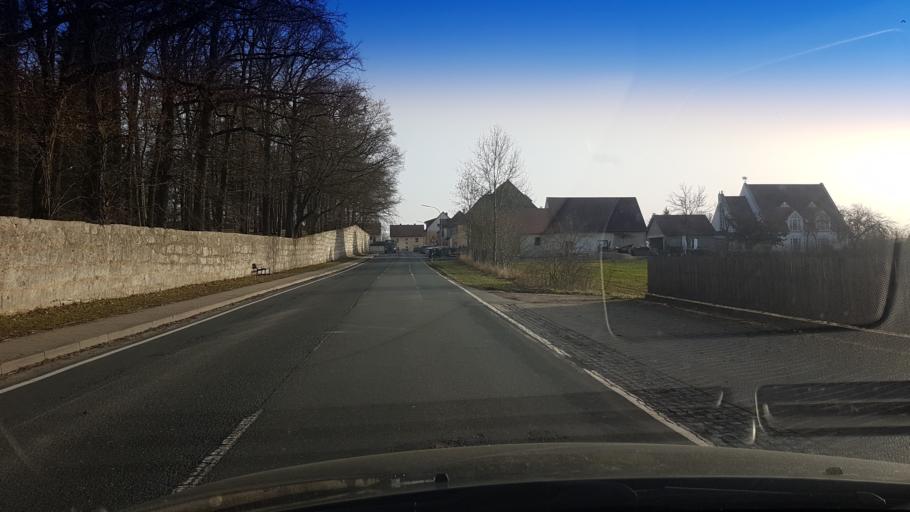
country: DE
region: Bavaria
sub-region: Upper Franconia
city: Pommersfelden
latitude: 49.7643
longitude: 10.8163
